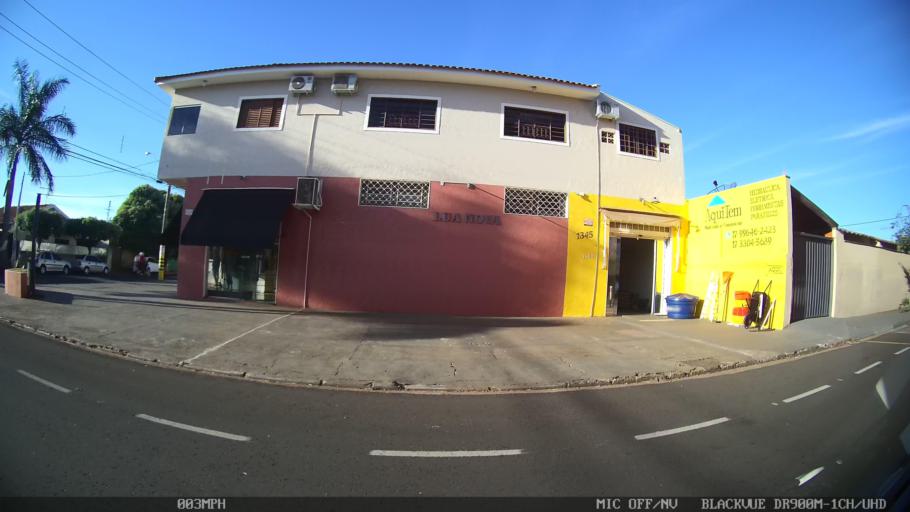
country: BR
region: Sao Paulo
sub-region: Sao Jose Do Rio Preto
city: Sao Jose do Rio Preto
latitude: -20.8302
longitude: -49.3746
